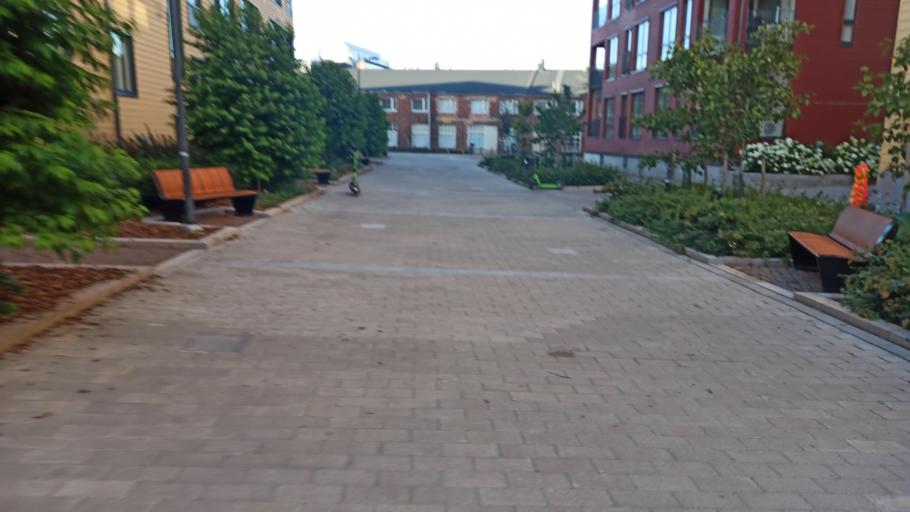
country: FI
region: Varsinais-Suomi
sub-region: Turku
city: Turku
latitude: 60.4384
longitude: 22.2351
